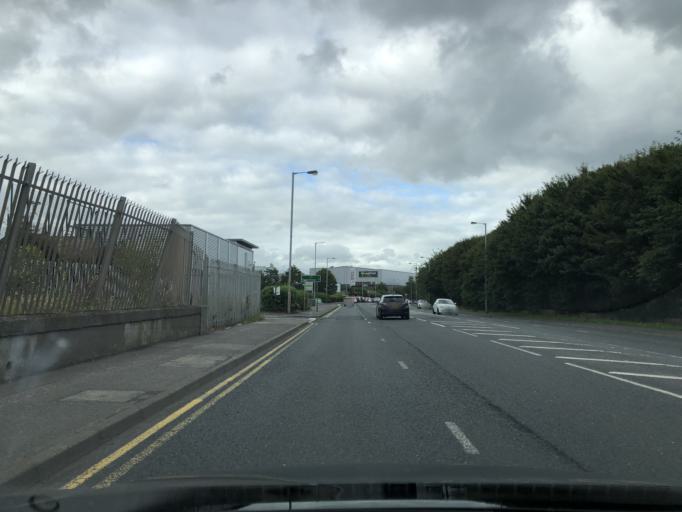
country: GB
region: Northern Ireland
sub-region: Newtownabbey District
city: Newtownabbey
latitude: 54.6499
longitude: -5.9188
